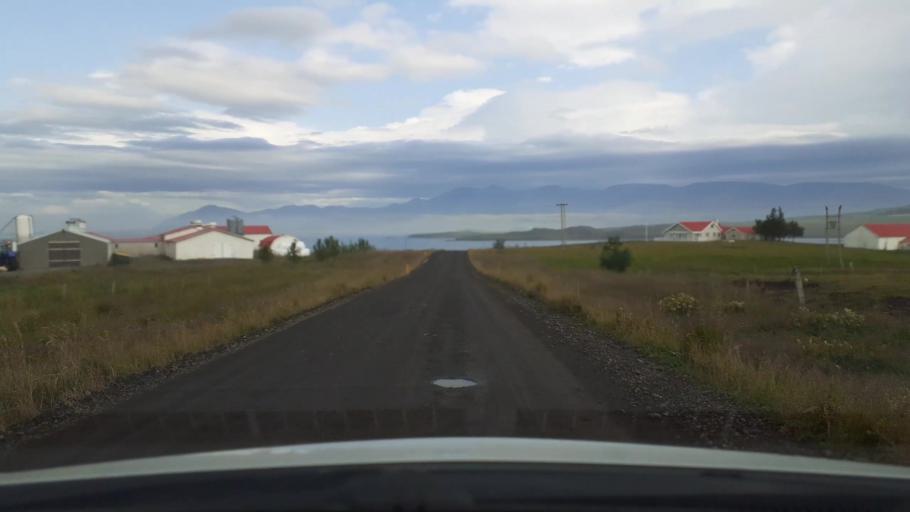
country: IS
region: Capital Region
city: Mosfellsbaer
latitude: 64.3267
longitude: -21.6516
